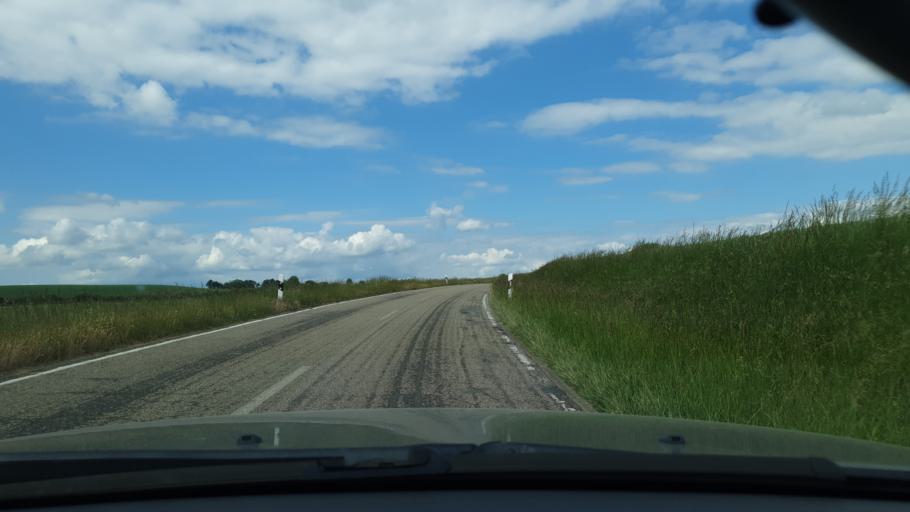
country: DE
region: Rheinland-Pfalz
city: Contwig
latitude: 49.2584
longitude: 7.4303
